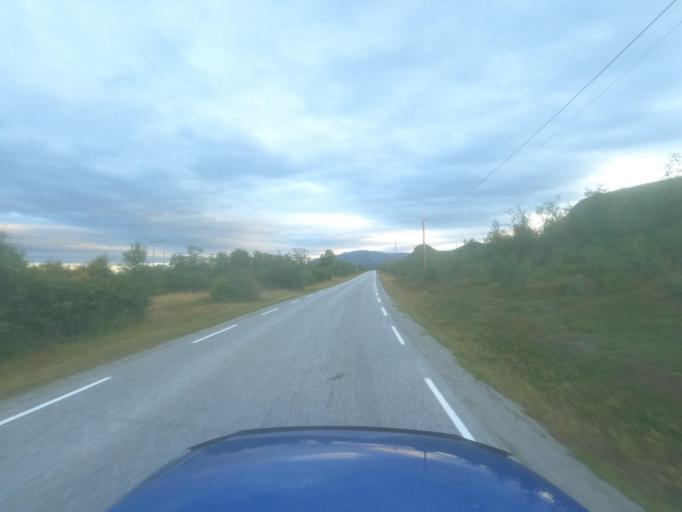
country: NO
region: Finnmark Fylke
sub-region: Porsanger
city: Lakselv
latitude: 70.1929
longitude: 24.9170
